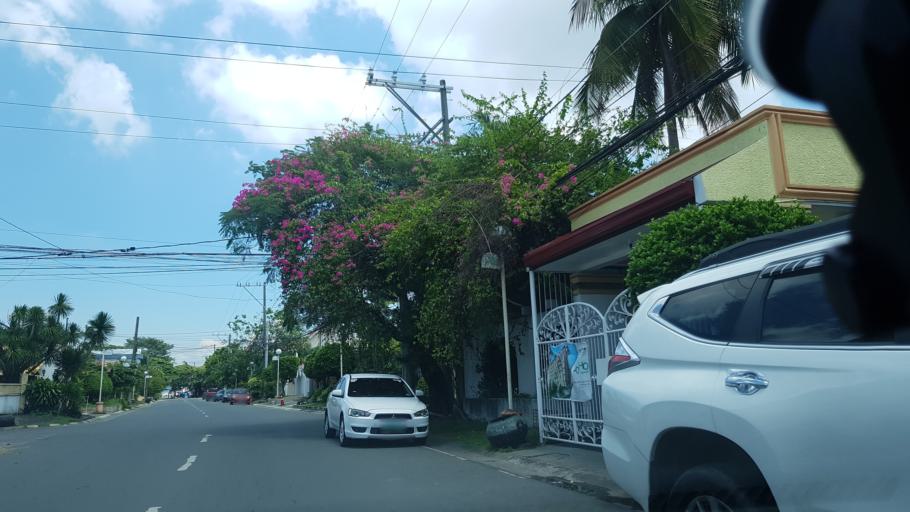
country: PH
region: Calabarzon
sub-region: Province of Rizal
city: Las Pinas
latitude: 14.4368
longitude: 120.9846
